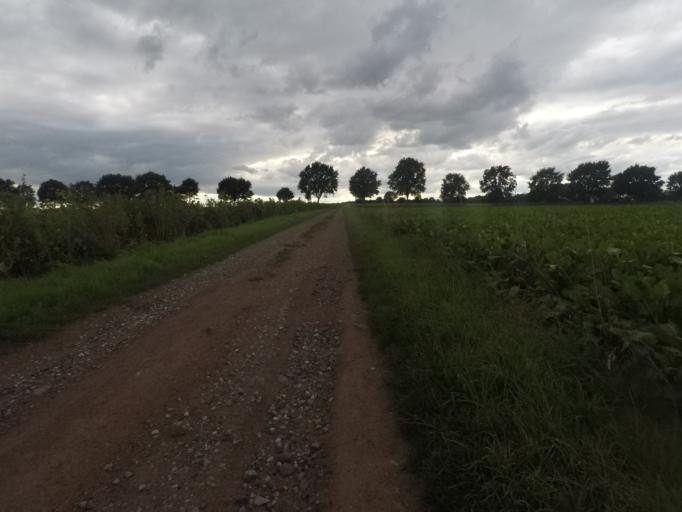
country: DE
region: North Rhine-Westphalia
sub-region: Regierungsbezirk Detmold
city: Hiddenhausen
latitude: 52.1570
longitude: 8.6177
